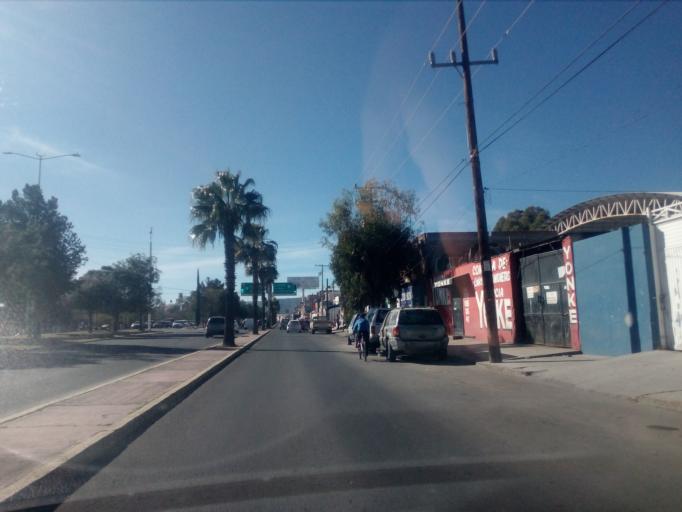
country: MX
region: Durango
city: Victoria de Durango
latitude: 23.9895
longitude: -104.6641
